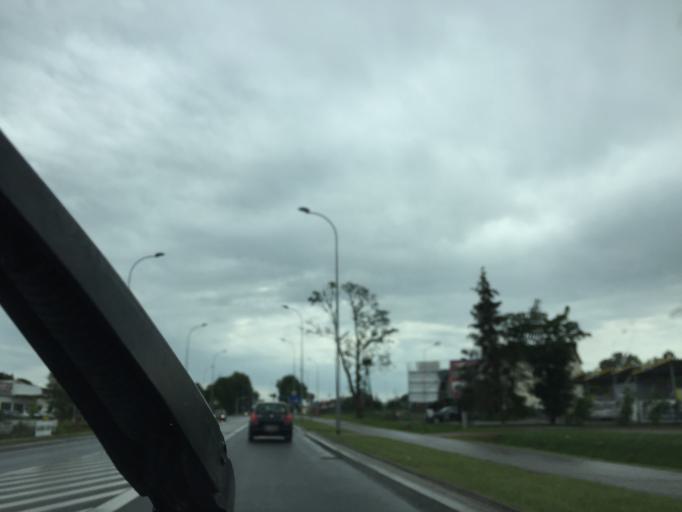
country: PL
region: Podlasie
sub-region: Bialystok
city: Bialystok
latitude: 53.0981
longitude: 23.2306
